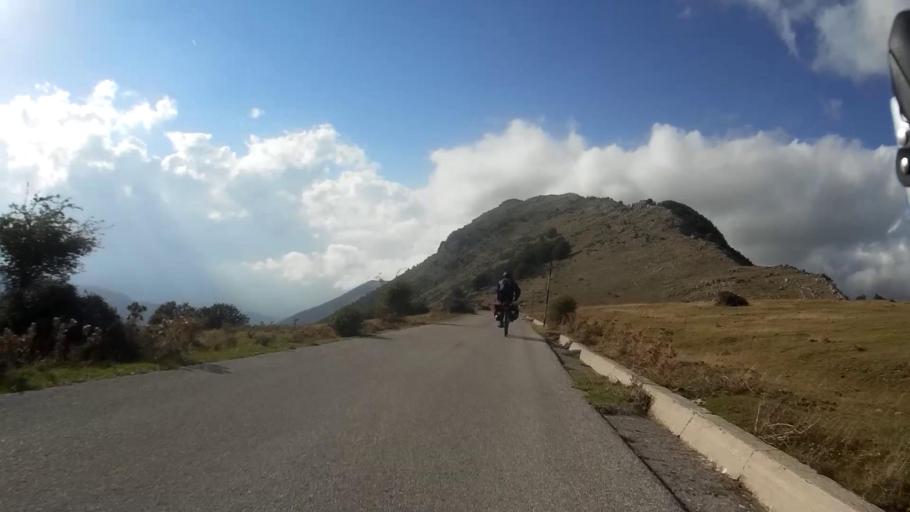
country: IT
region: Basilicate
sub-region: Provincia di Potenza
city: Viggianello
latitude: 39.9570
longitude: 16.1399
